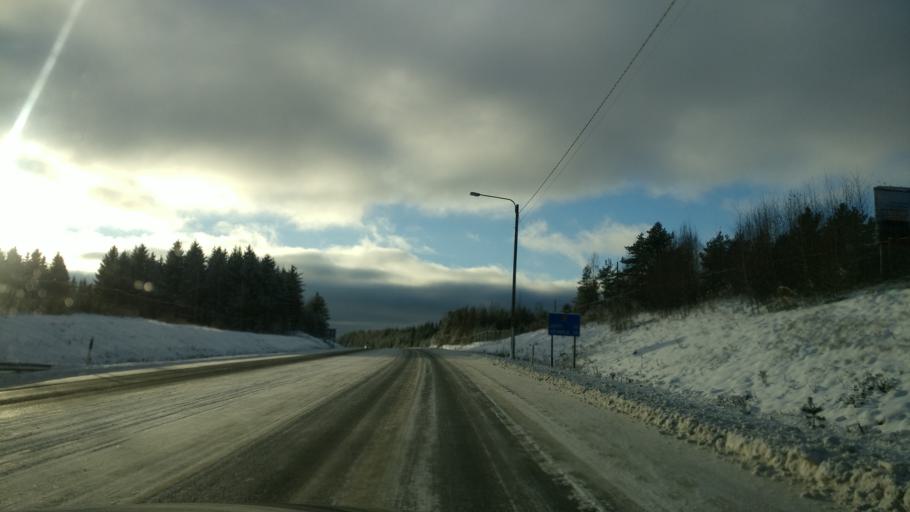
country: FI
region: Southern Savonia
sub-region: Mikkeli
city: Pertunmaa
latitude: 61.4159
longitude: 26.4215
